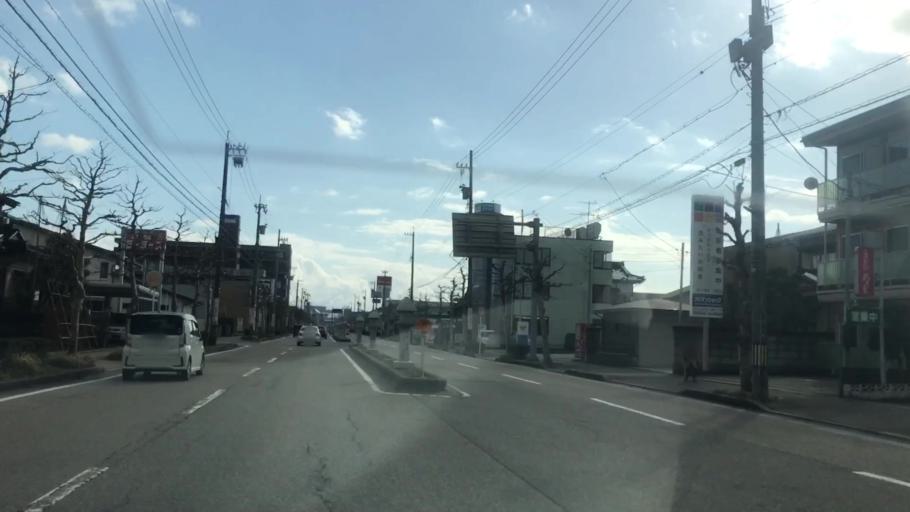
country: JP
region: Toyama
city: Takaoka
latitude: 36.7353
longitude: 137.0155
